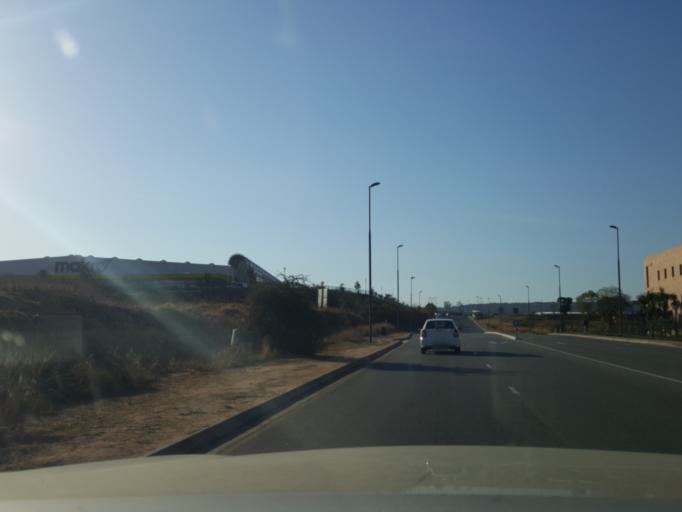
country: ZA
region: Mpumalanga
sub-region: Ehlanzeni District
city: Nelspruit
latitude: -25.4401
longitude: 30.9618
